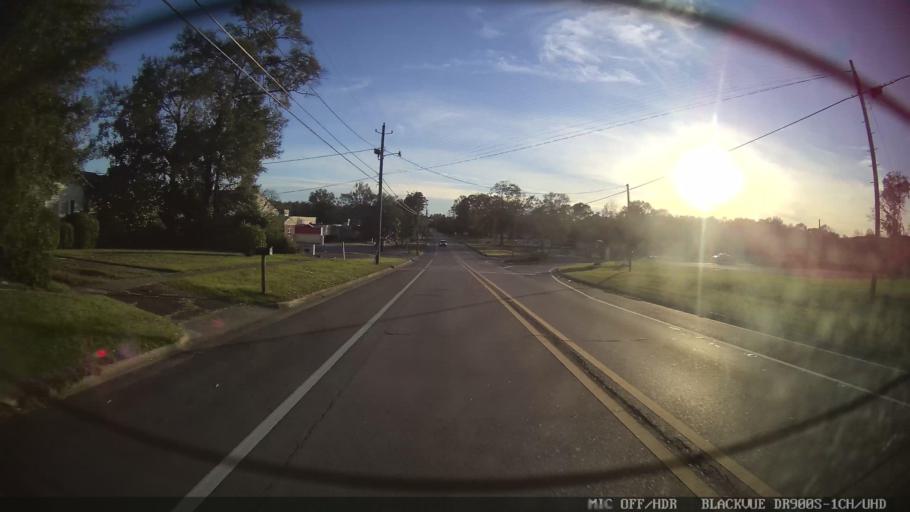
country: US
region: Mississippi
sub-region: Lamar County
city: Lumberton
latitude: 30.9986
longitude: -89.4536
